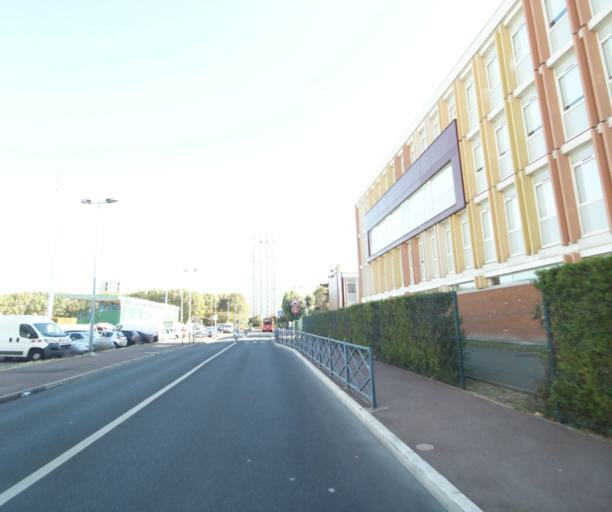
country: FR
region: Ile-de-France
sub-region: Departement des Hauts-de-Seine
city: Villeneuve-la-Garenne
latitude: 48.9397
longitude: 2.3277
